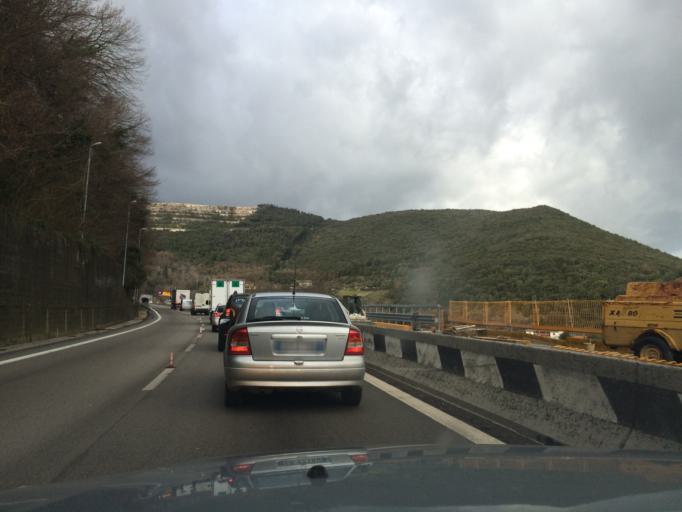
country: IT
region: Umbria
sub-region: Provincia di Terni
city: Narni Scalo
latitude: 42.5419
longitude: 12.4982
